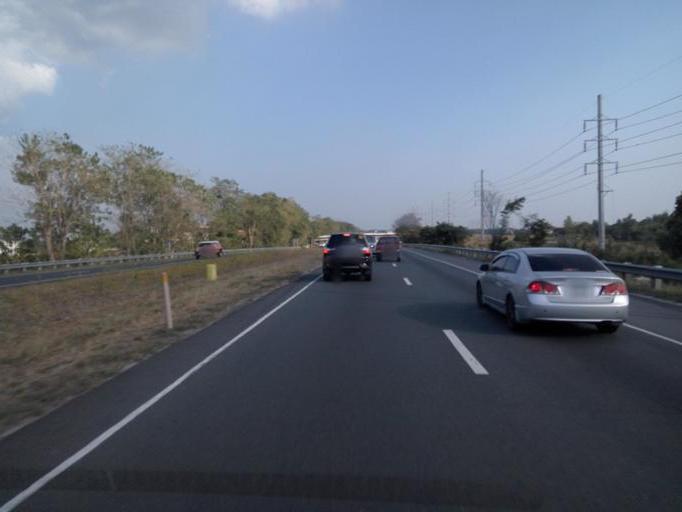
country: PH
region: Central Luzon
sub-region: Province of Pampanga
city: Acli
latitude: 15.1108
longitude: 120.6597
